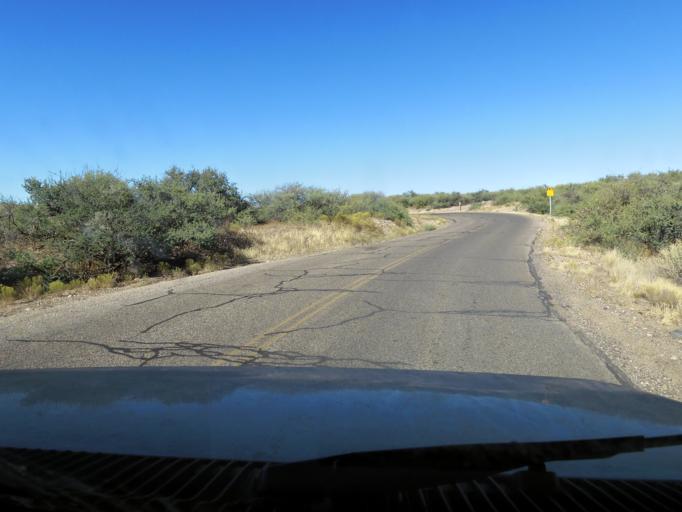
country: US
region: Arizona
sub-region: Yavapai County
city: Camp Verde
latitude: 34.5985
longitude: -111.8939
